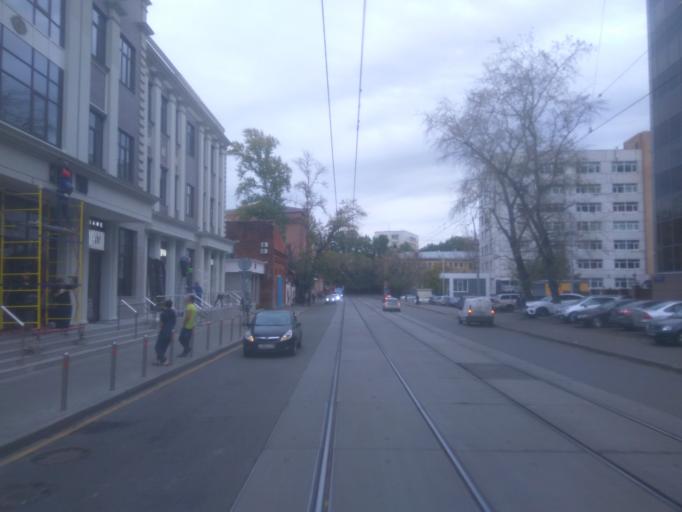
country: RU
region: Moscow
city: Sokol'niki
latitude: 55.7765
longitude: 37.6757
